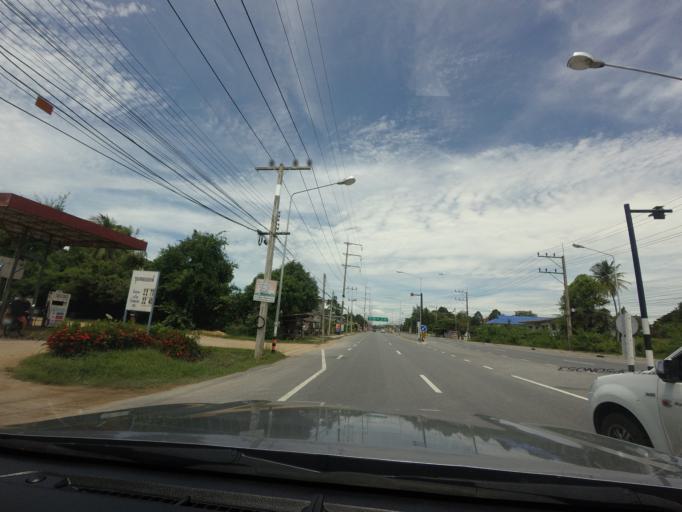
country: TH
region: Songkhla
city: Krasae Sin
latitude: 7.6047
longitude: 100.4001
